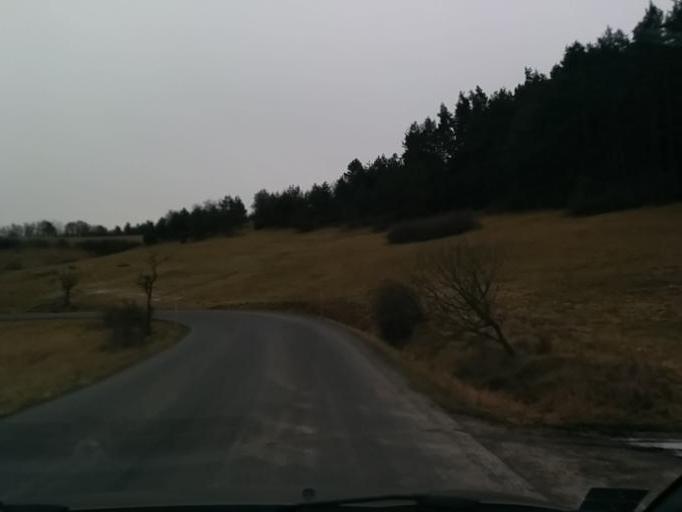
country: SK
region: Banskobystricky
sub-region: Okres Banska Bystrica
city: Zvolen
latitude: 48.6374
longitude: 19.1914
